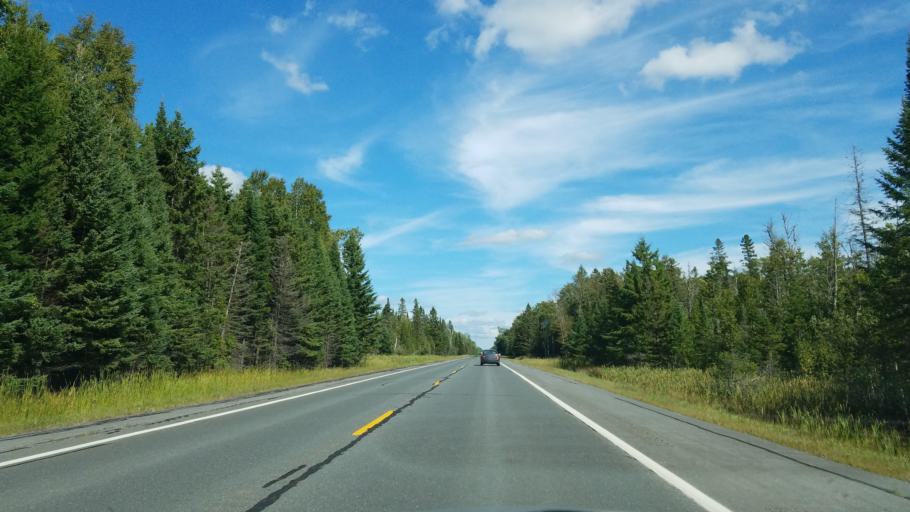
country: US
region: Michigan
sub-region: Baraga County
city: L'Anse
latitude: 46.5788
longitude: -88.4315
